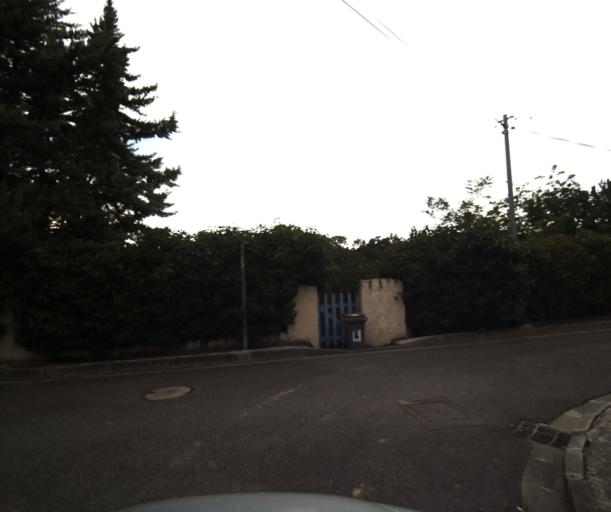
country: FR
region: Midi-Pyrenees
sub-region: Departement de la Haute-Garonne
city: Le Fauga
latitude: 43.4151
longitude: 1.3103
